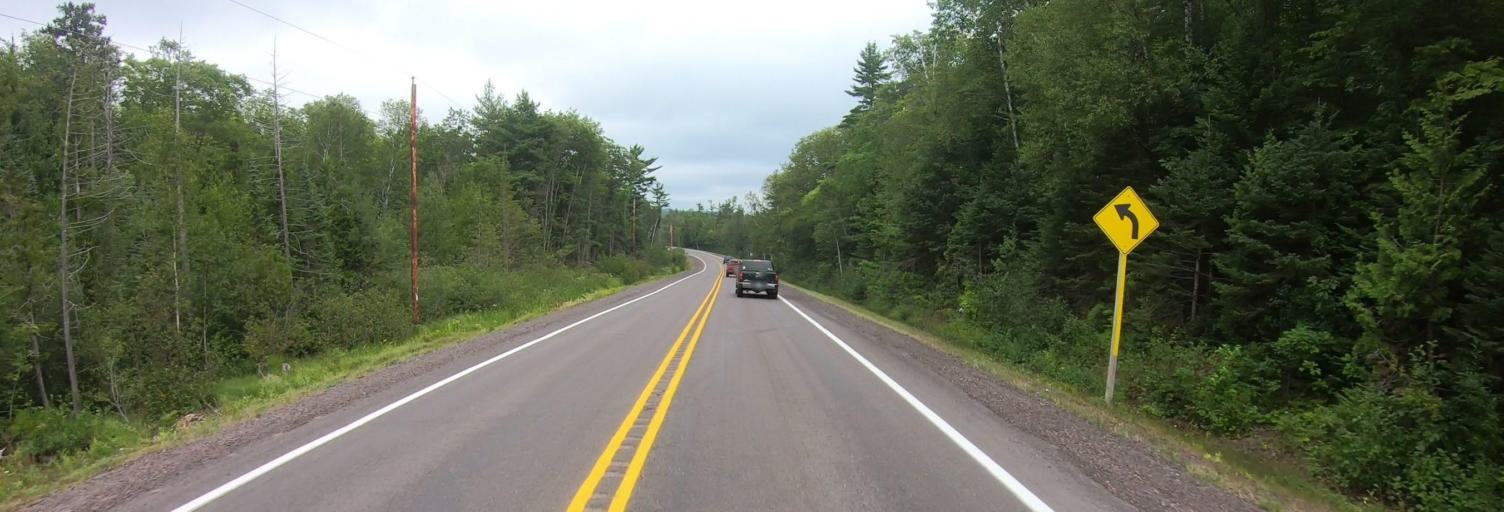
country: US
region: Michigan
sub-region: Keweenaw County
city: Eagle River
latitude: 47.4106
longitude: -88.1718
